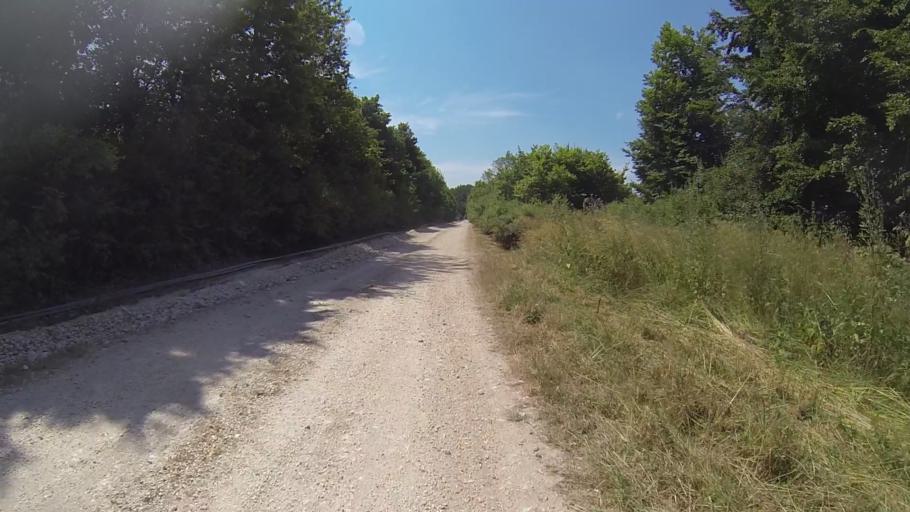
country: DE
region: Baden-Wuerttemberg
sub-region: Regierungsbezirk Stuttgart
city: Giengen an der Brenz
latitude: 48.6438
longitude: 10.2167
